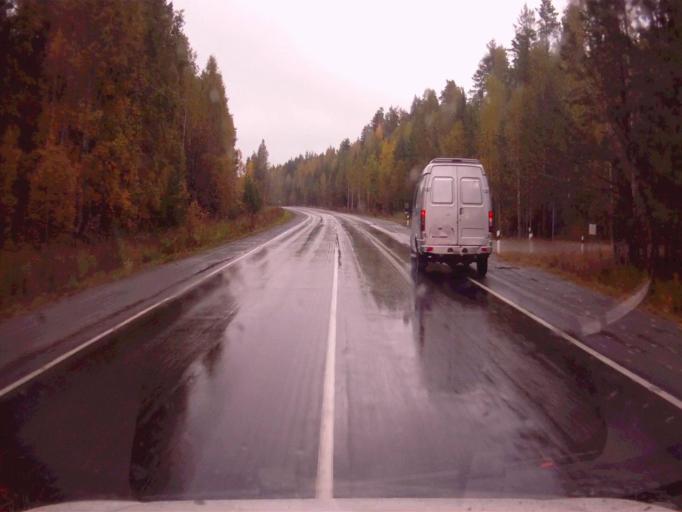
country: RU
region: Chelyabinsk
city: Tayginka
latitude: 55.5679
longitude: 60.6507
